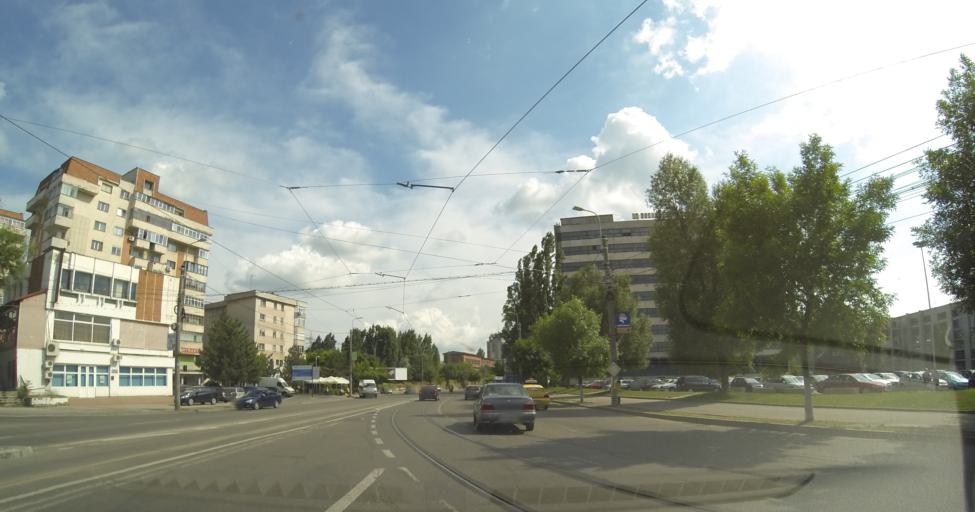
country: RO
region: Dolj
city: Craiova
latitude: 44.3131
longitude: 23.8344
